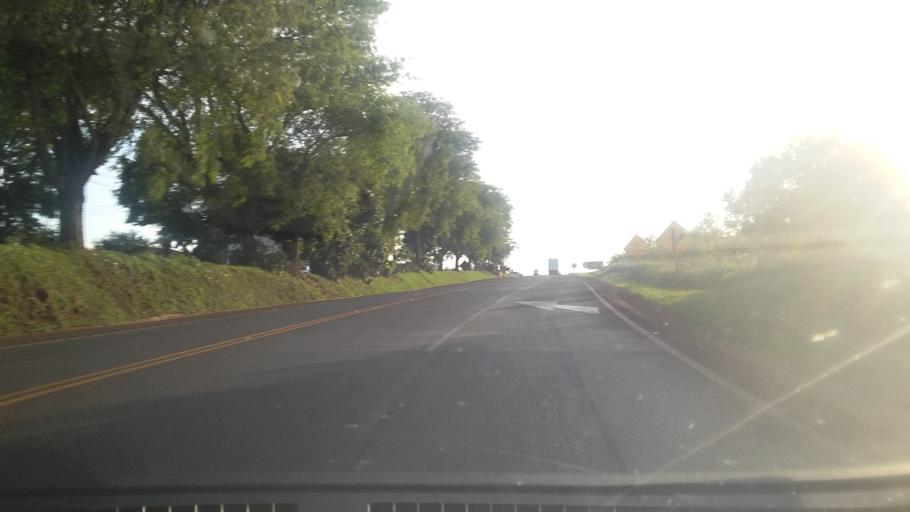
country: BR
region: Parana
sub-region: Bandeirantes
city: Bandeirantes
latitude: -23.1739
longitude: -50.6230
